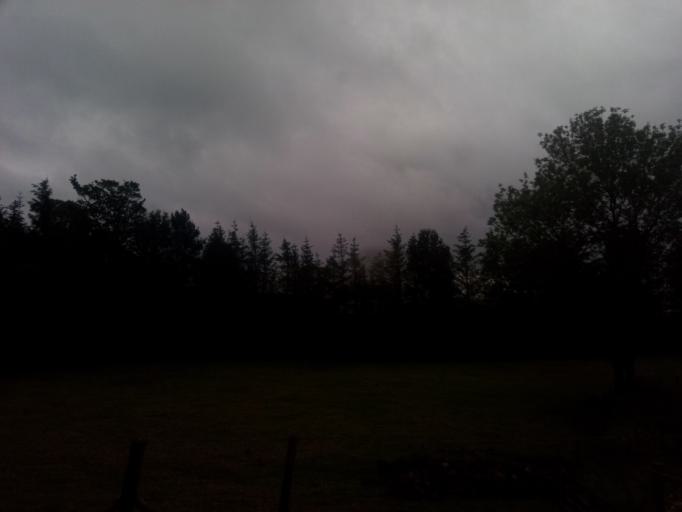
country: GB
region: England
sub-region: North Yorkshire
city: Settle
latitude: 54.0062
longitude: -2.2125
